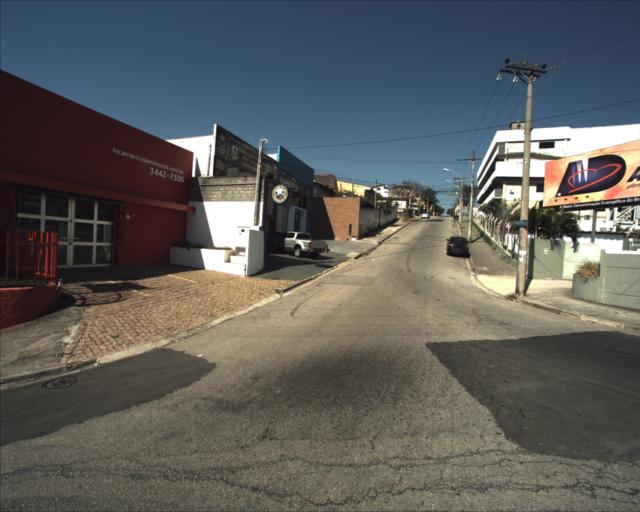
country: BR
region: Sao Paulo
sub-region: Sorocaba
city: Sorocaba
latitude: -23.5012
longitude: -47.4777
